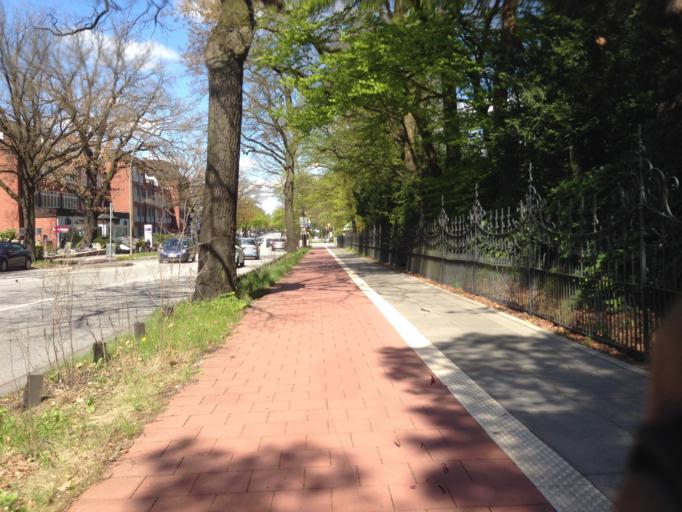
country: DE
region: Hamburg
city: Ohlsdorf
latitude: 53.6183
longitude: 10.0344
